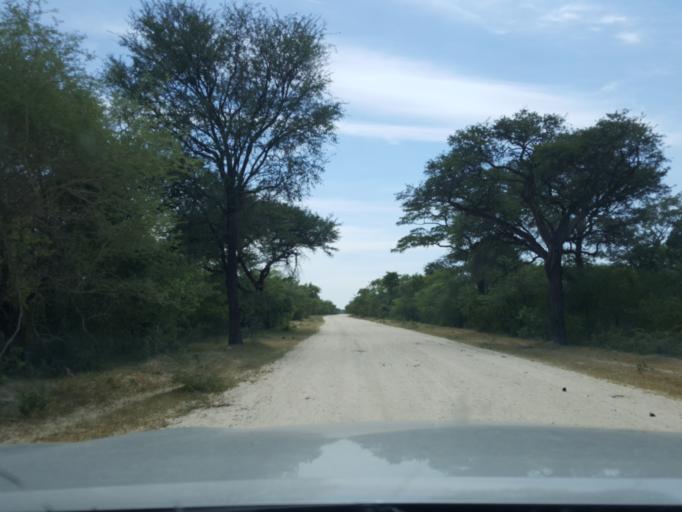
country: BW
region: North West
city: Shakawe
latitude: -18.6164
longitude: 21.9785
